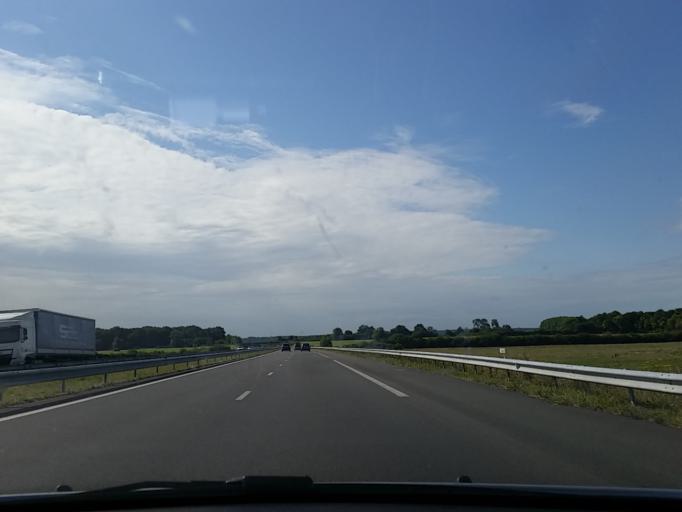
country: FR
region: Centre
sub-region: Departement du Cher
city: Orval
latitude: 46.8100
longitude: 2.4123
